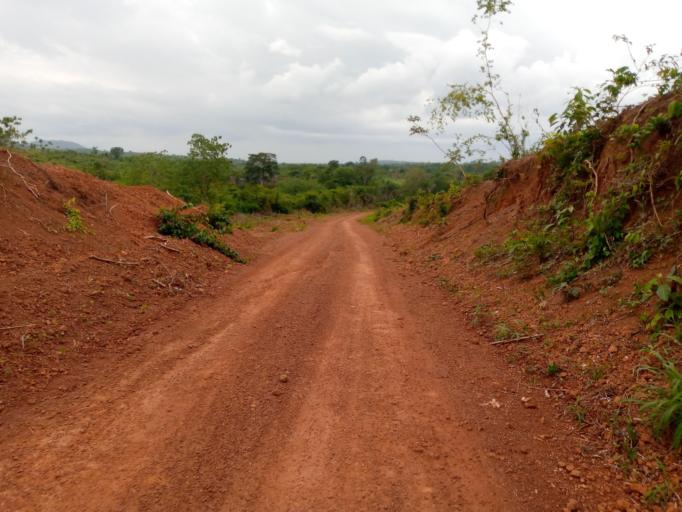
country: SL
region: Southern Province
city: Moyamba
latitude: 8.0778
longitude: -12.4532
